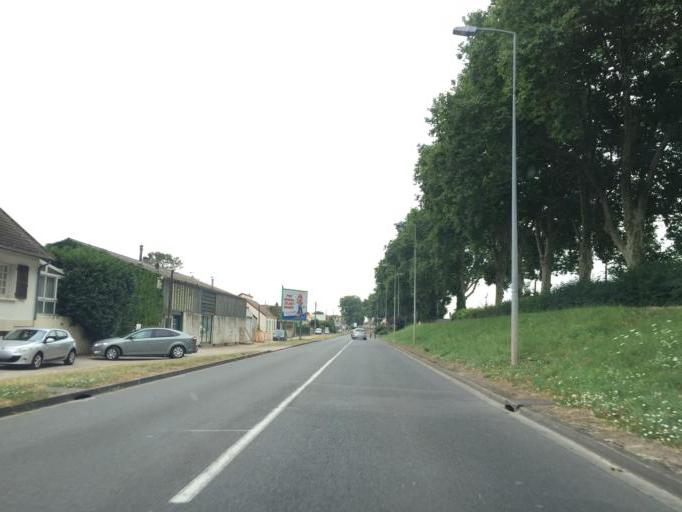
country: FR
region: Auvergne
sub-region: Departement de l'Allier
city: Moulins
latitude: 46.5719
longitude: 3.3203
